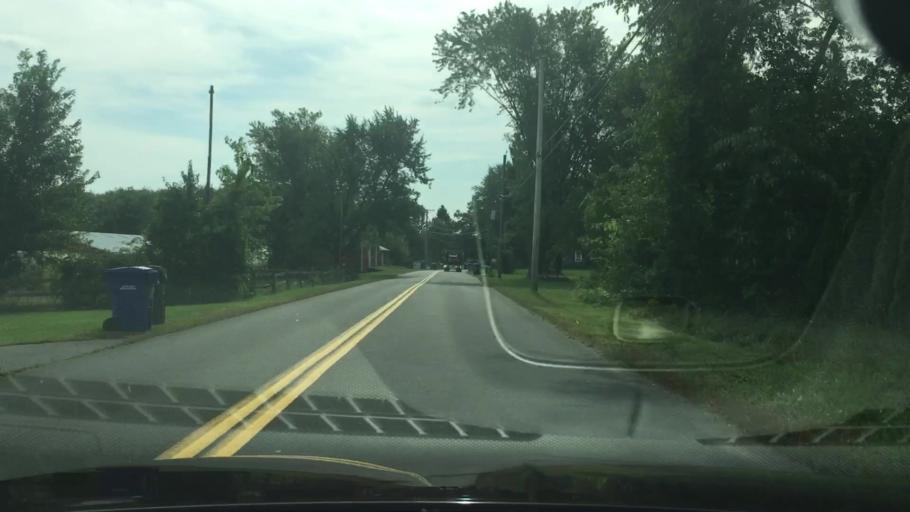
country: US
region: Connecticut
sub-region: Tolland County
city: Ellington
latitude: 41.9390
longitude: -72.4789
